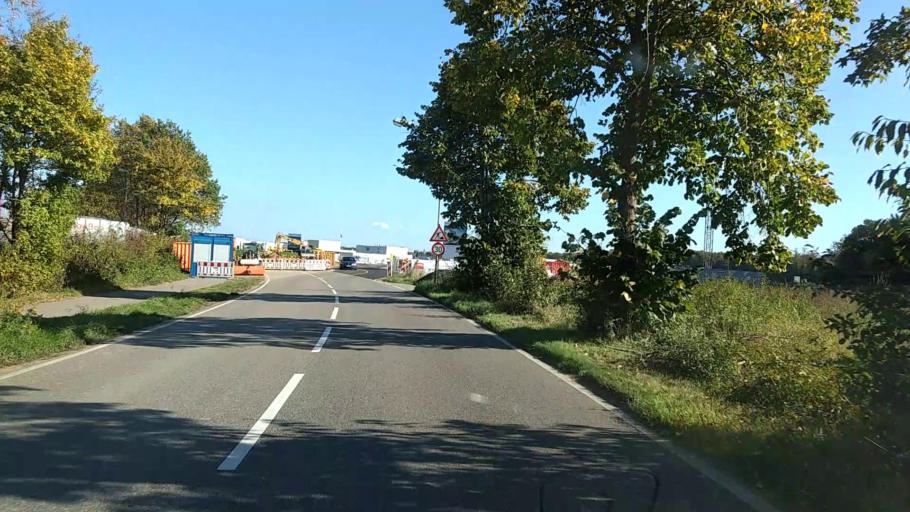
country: DE
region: North Rhine-Westphalia
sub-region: Regierungsbezirk Koln
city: Kerpen
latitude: 50.8930
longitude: 6.6654
